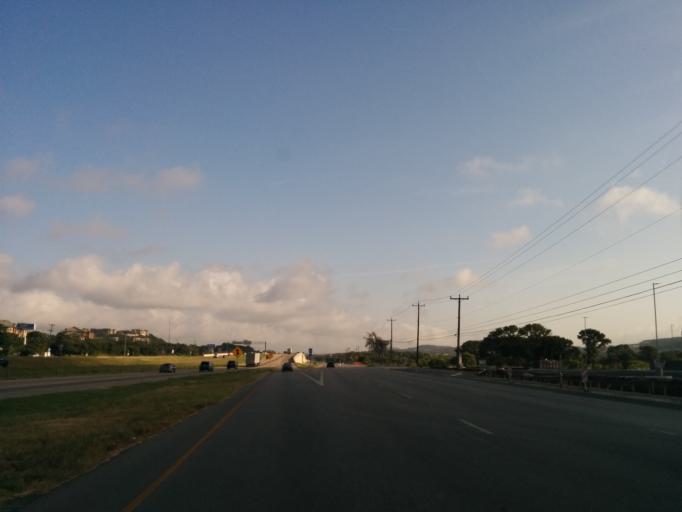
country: US
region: Texas
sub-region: Bexar County
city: Cross Mountain
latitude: 29.6199
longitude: -98.6077
